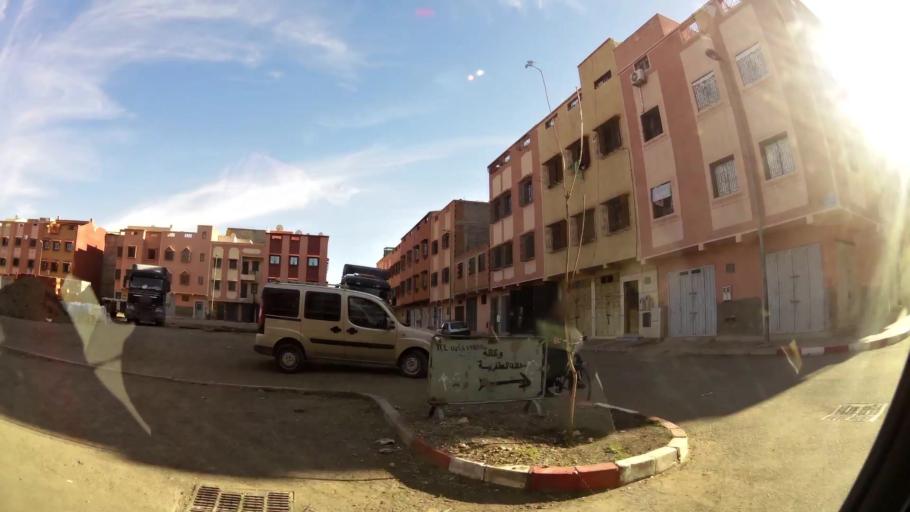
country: MA
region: Marrakech-Tensift-Al Haouz
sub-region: Marrakech
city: Marrakesh
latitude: 31.6242
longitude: -8.0687
